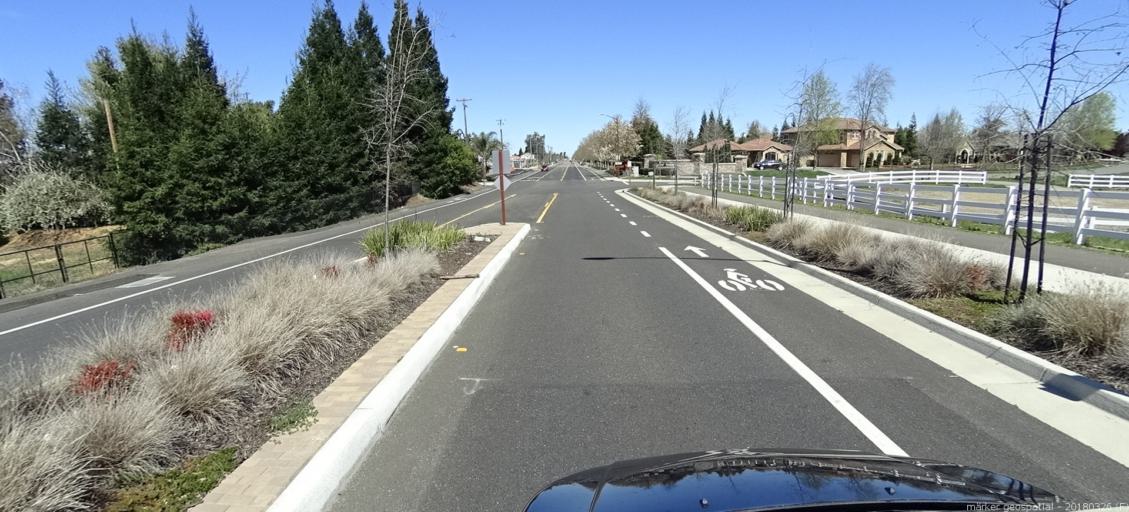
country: US
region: California
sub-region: Sacramento County
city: Vineyard
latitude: 38.4642
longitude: -121.3160
